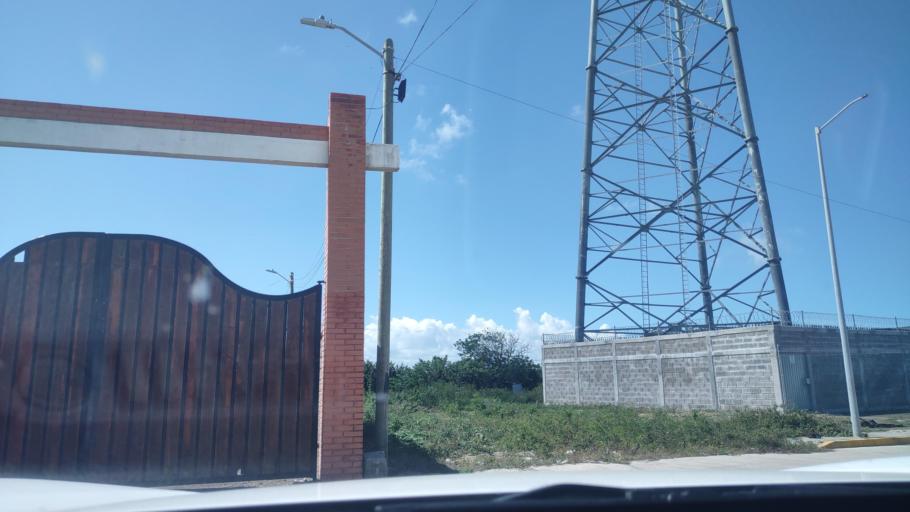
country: MX
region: Veracruz
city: Heroica Alvarado
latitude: 18.7818
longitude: -95.7733
